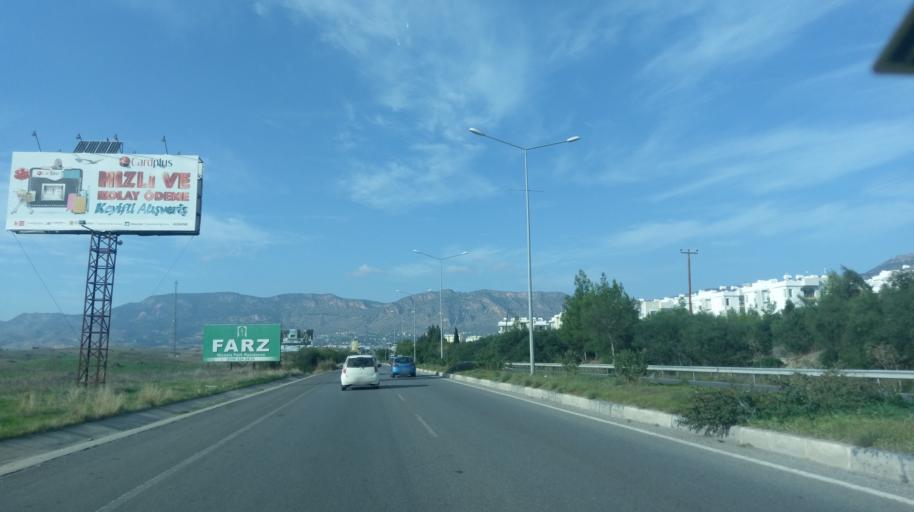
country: CY
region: Keryneia
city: Kyrenia
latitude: 35.2536
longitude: 33.3015
